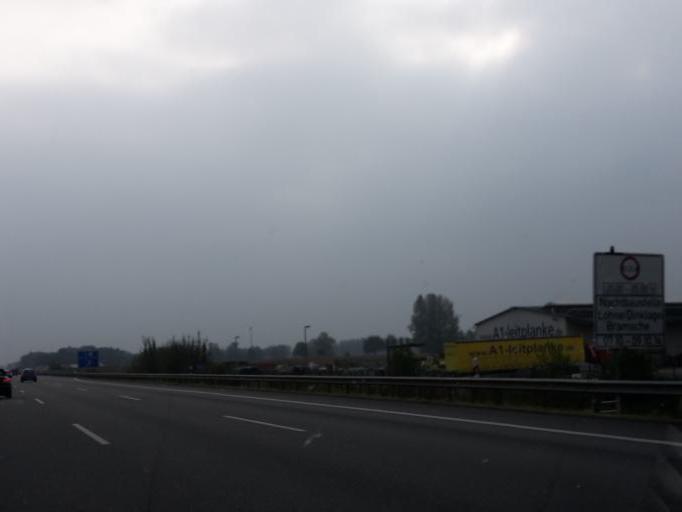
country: DE
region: Lower Saxony
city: Bakum
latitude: 52.7197
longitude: 8.1727
